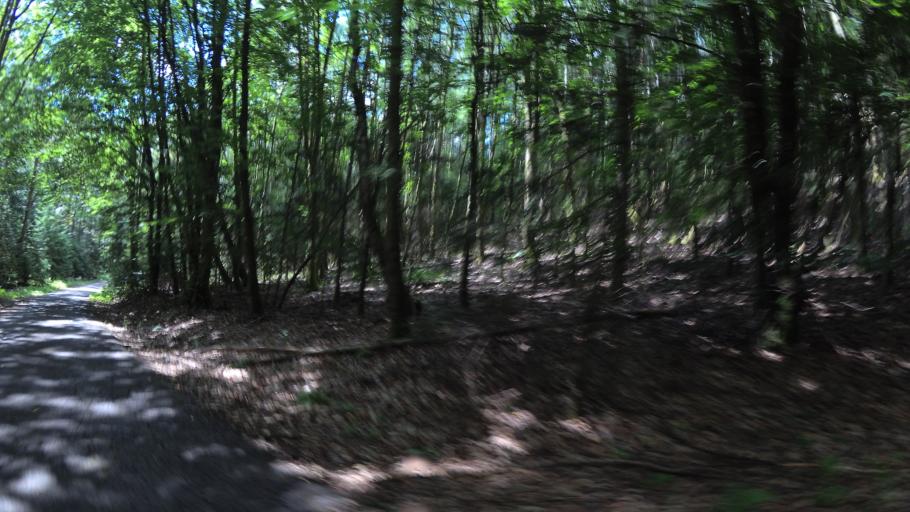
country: DE
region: Saarland
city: Weiskirchen
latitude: 49.5583
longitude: 6.7802
